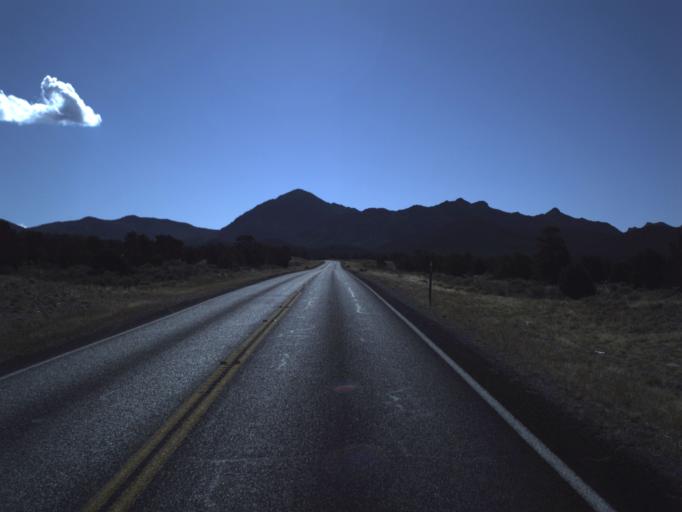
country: US
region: Utah
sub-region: Washington County
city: Enterprise
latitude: 37.6210
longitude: -113.4152
